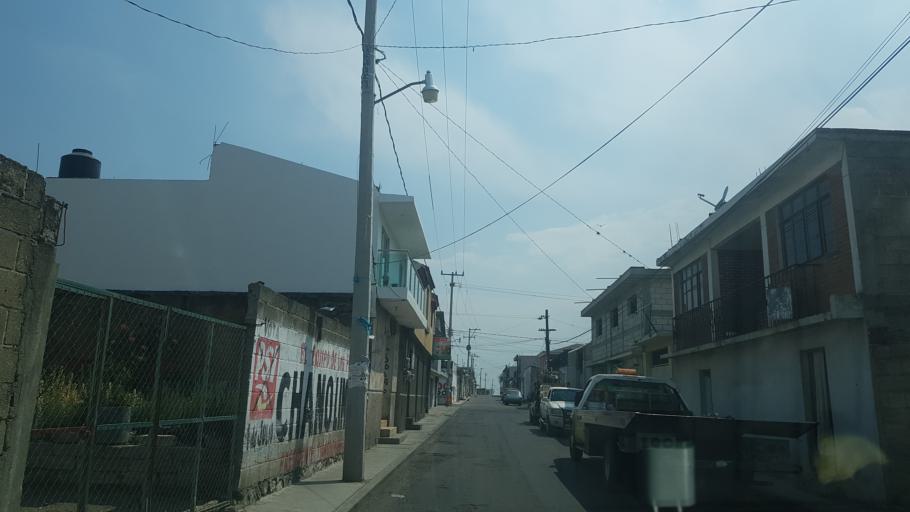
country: MX
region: Puebla
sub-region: Tianguismanalco
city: San Martin Tlapala
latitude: 18.9741
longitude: -98.4491
